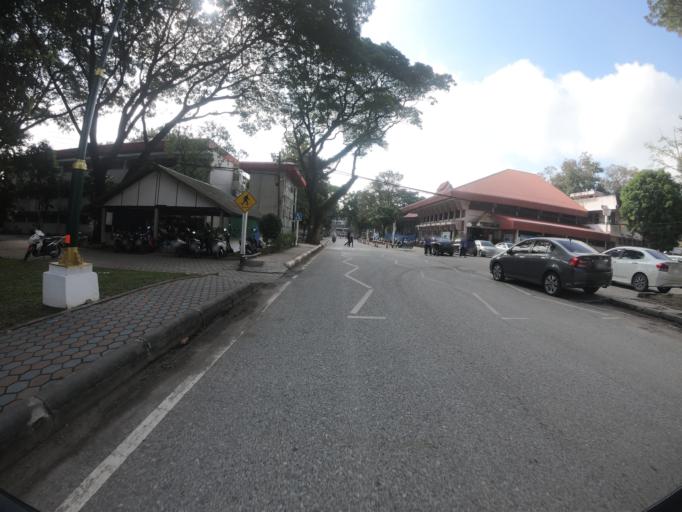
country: TH
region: Chiang Mai
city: Chiang Mai
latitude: 18.7940
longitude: 98.9544
